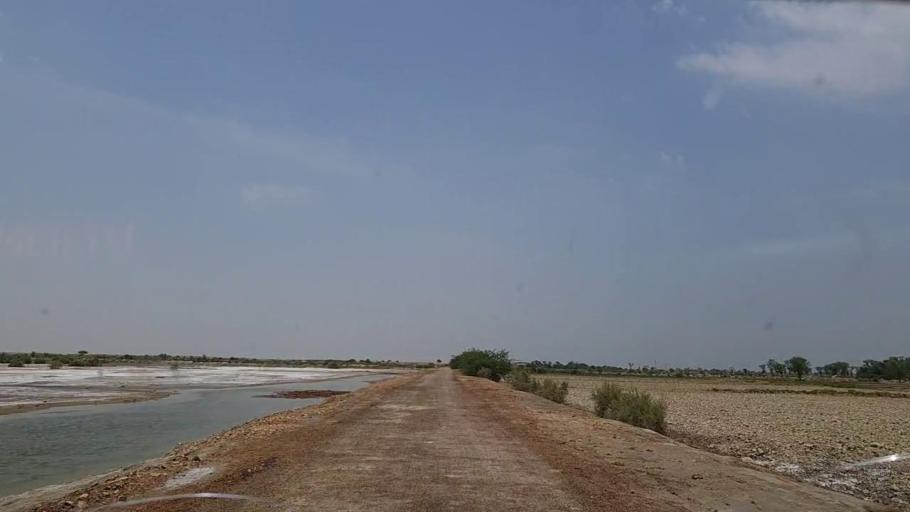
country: PK
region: Sindh
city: Phulji
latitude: 26.8685
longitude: 67.6530
